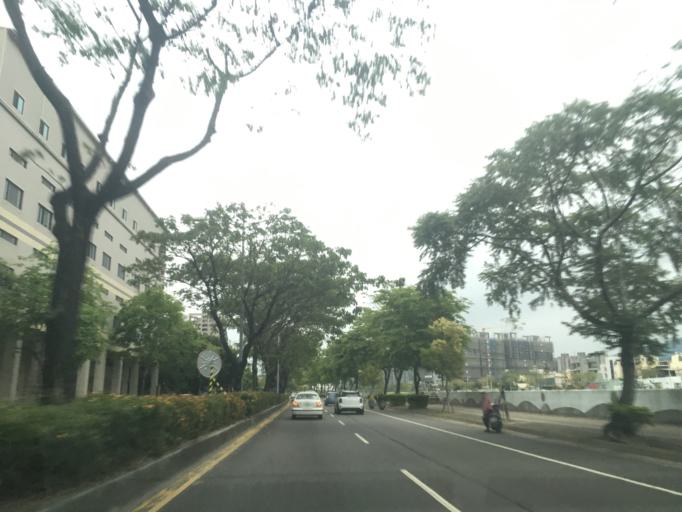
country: TW
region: Taiwan
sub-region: Taichung City
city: Taichung
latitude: 24.1534
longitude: 120.7251
